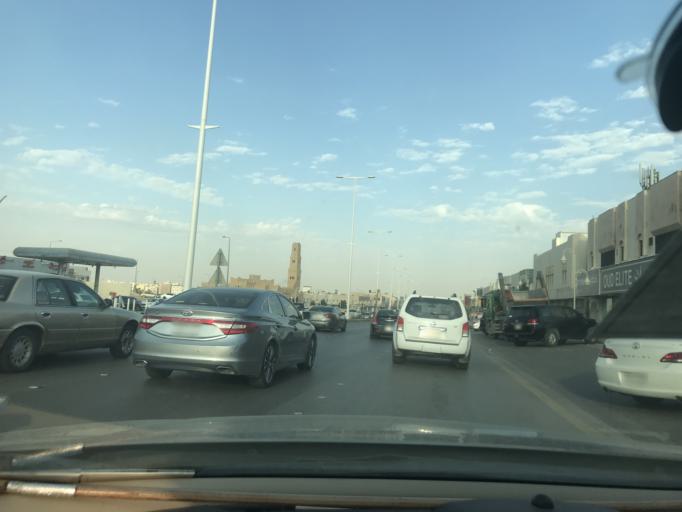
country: SA
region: Ar Riyad
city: Riyadh
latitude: 24.7449
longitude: 46.7558
